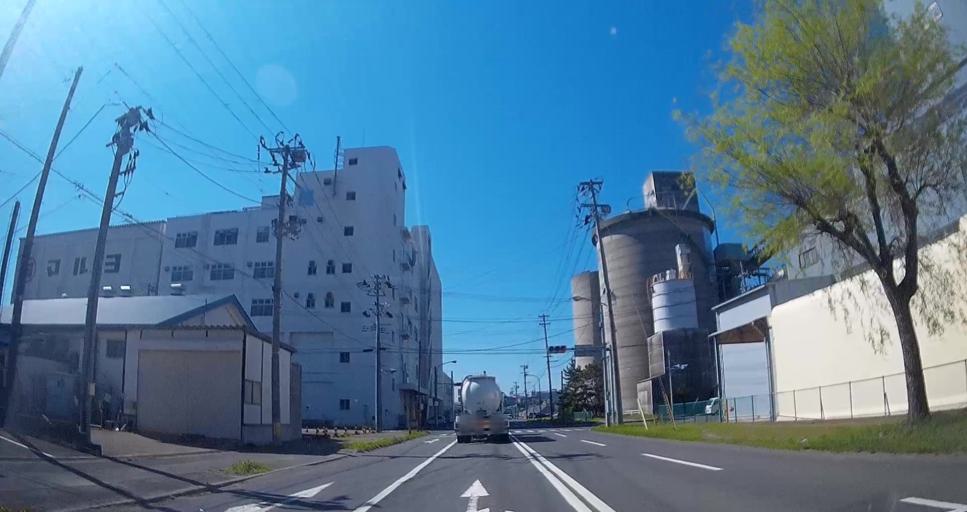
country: JP
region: Aomori
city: Hachinohe
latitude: 40.5278
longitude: 141.5447
